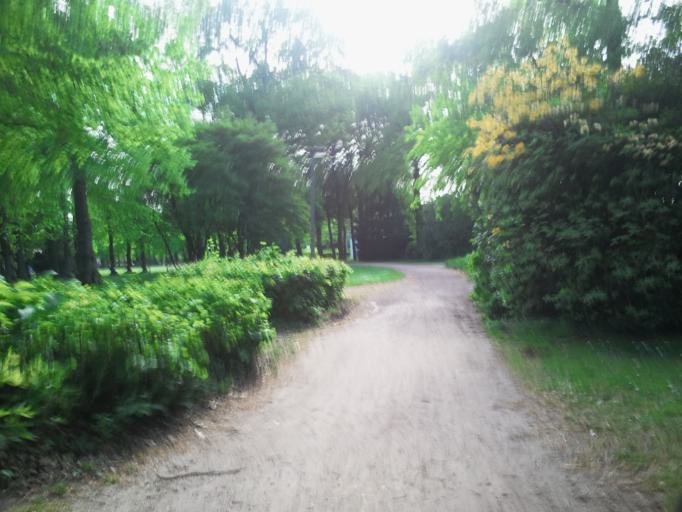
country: DE
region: Lower Saxony
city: Nienburg
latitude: 52.6307
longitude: 9.2241
